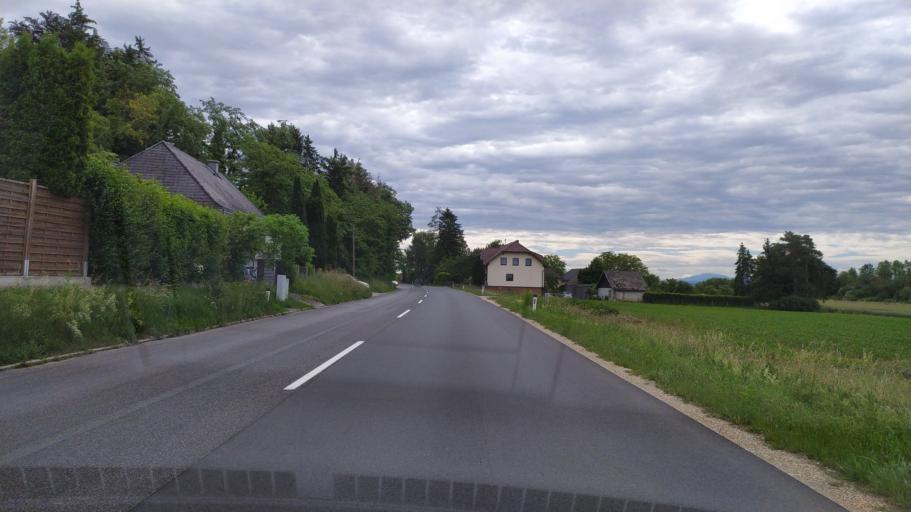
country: AT
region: Upper Austria
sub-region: Politischer Bezirk Perg
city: Perg
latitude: 48.2517
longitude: 14.5996
